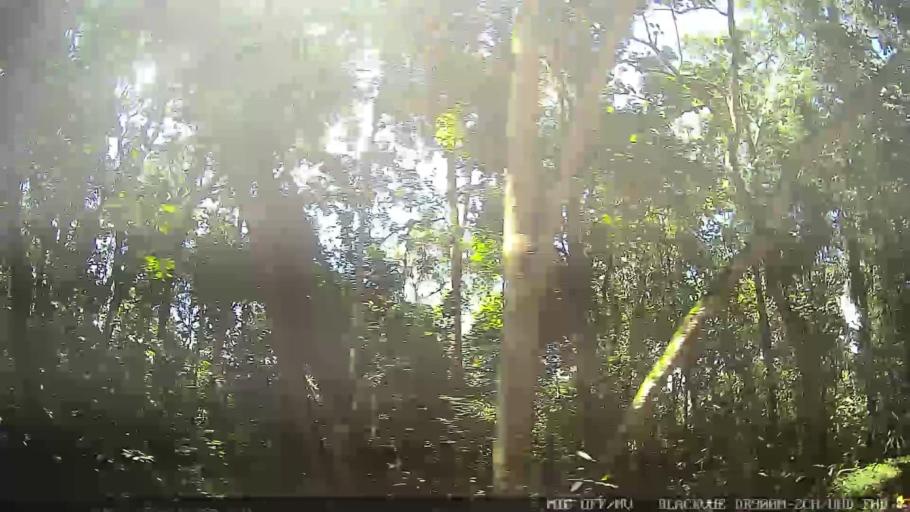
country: BR
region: Sao Paulo
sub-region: Mogi das Cruzes
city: Mogi das Cruzes
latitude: -23.5962
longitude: -46.1515
